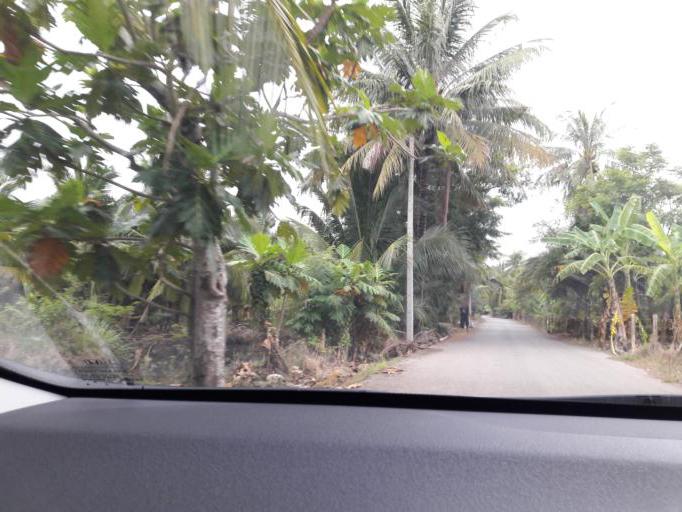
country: TH
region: Samut Sakhon
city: Ban Phaeo
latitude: 13.5672
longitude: 100.0298
